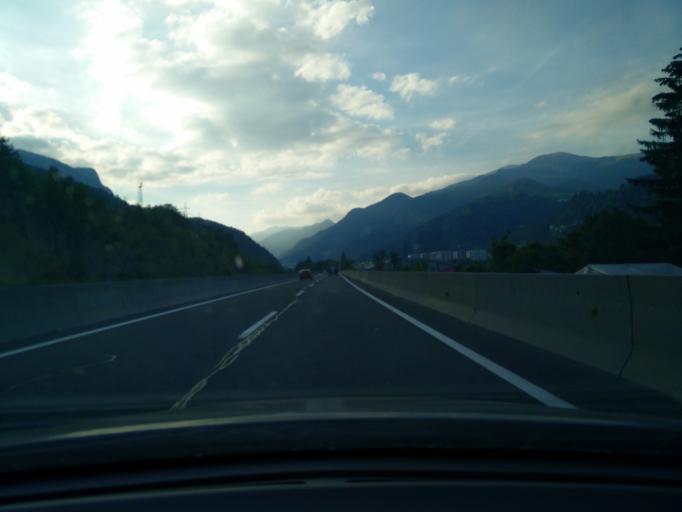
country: SI
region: Jesenice
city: Jesenice
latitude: 46.4303
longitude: 14.0549
